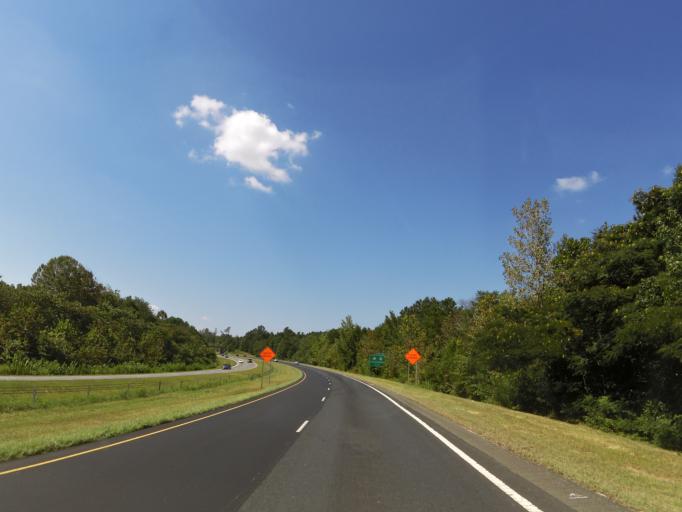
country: US
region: North Carolina
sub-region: Lincoln County
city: Lincolnton
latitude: 35.4657
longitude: -81.2201
